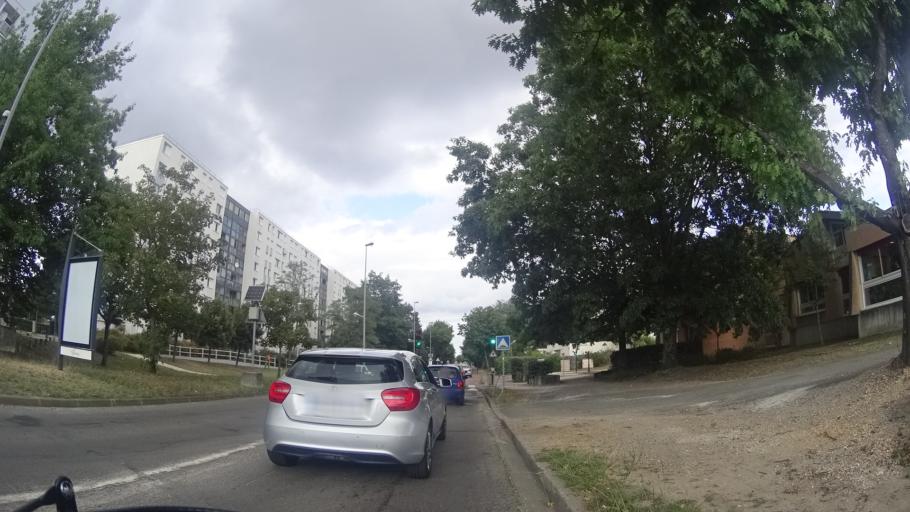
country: FR
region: Aquitaine
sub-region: Departement de la Gironde
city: Talence
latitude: 44.7919
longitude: -0.5860
